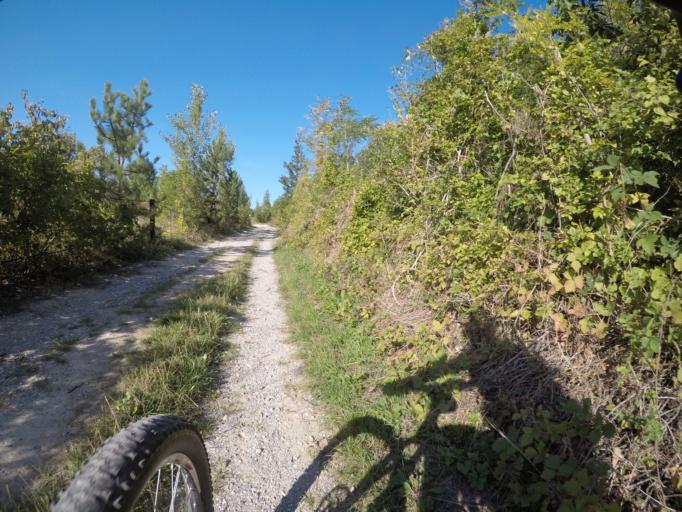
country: AT
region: Lower Austria
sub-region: Politischer Bezirk Bruck an der Leitha
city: Mannersdorf am Leithagebirge
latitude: 47.9639
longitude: 16.6123
